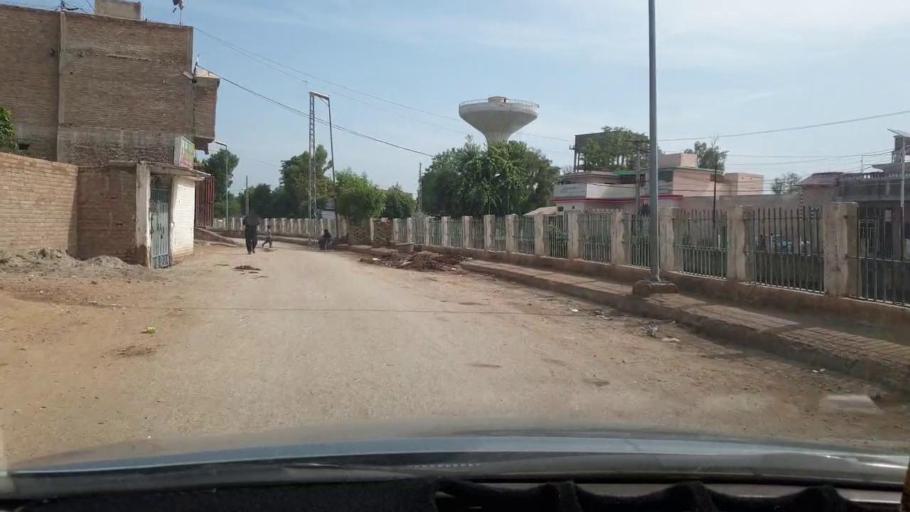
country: PK
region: Sindh
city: Khairpur
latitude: 27.5328
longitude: 68.7533
